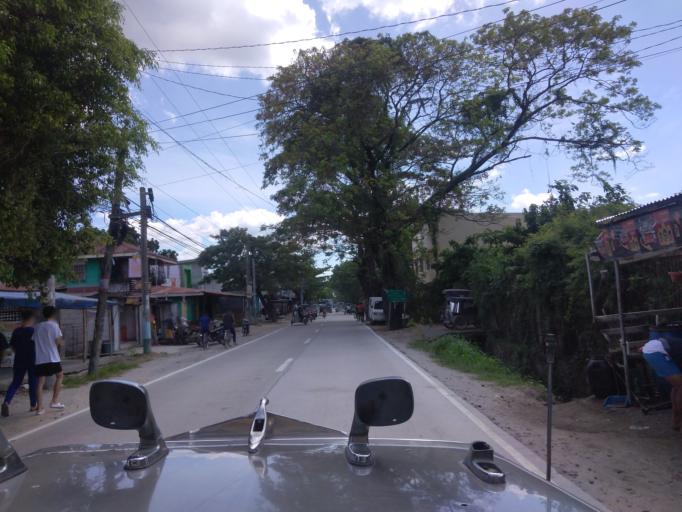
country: PH
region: Central Luzon
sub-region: Province of Pampanga
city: Santa Rita
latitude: 15.0104
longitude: 120.5931
